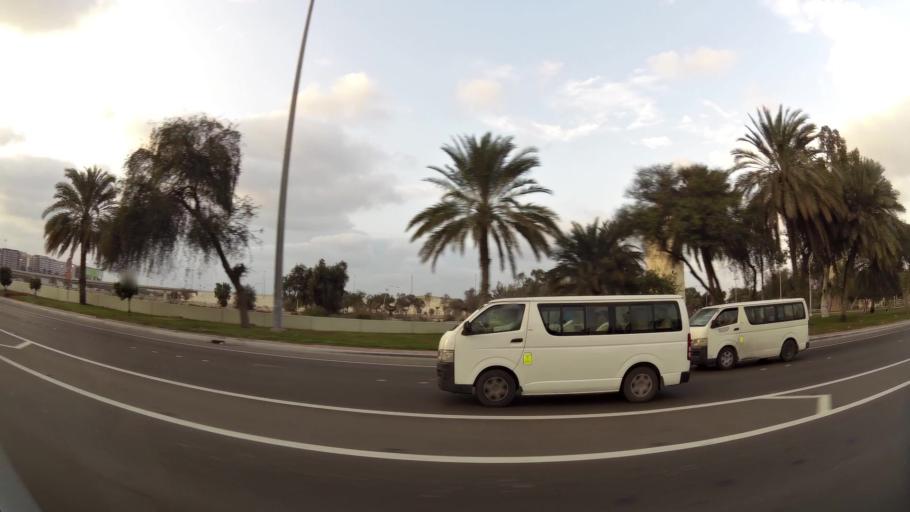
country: AE
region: Abu Dhabi
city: Abu Dhabi
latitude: 24.4201
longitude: 54.4812
